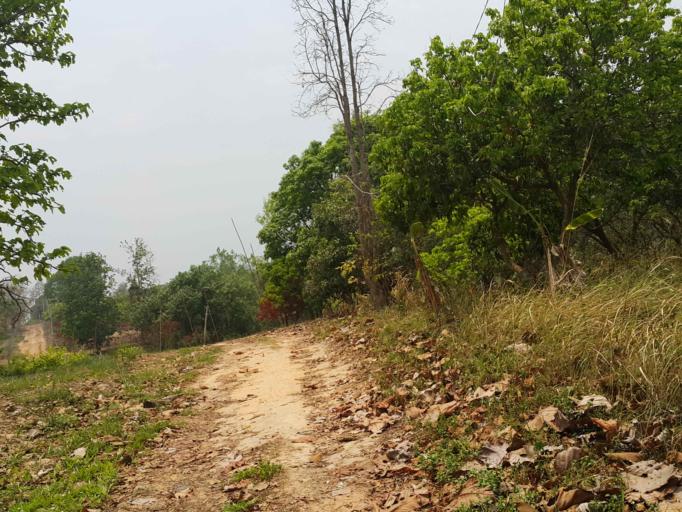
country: TH
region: Chiang Mai
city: San Sai
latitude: 18.9386
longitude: 99.0364
